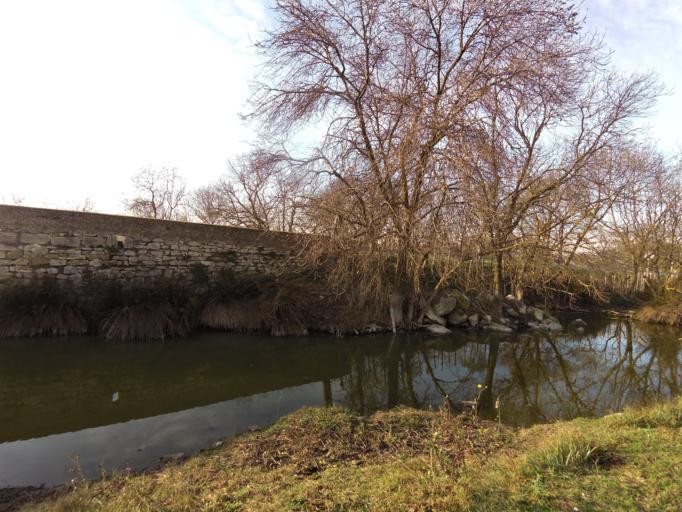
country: FR
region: Languedoc-Roussillon
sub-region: Departement du Gard
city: Aigues-Mortes
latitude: 43.5974
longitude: 4.2077
